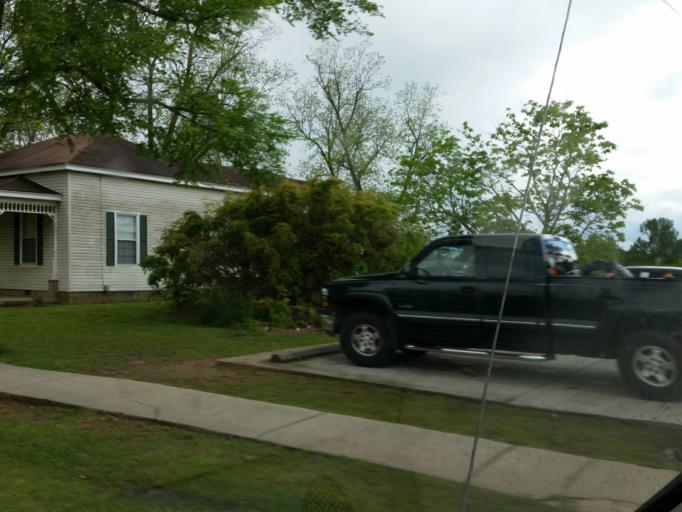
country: US
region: Georgia
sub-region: Lamar County
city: Barnesville
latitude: 33.1124
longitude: -84.1960
